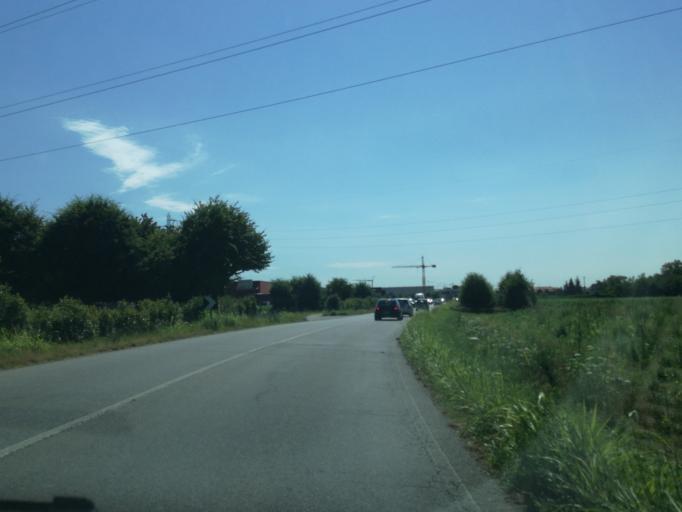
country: IT
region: Lombardy
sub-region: Provincia di Bergamo
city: Sotto il Monte Giovanni XXIII
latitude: 45.6950
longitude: 9.5097
